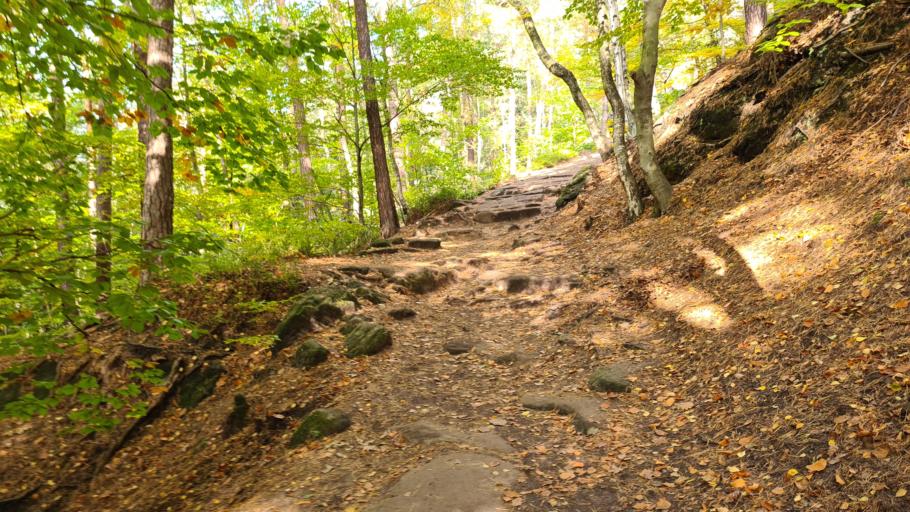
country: DE
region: Saxony
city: Konigstein
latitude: 50.8980
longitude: 14.0786
